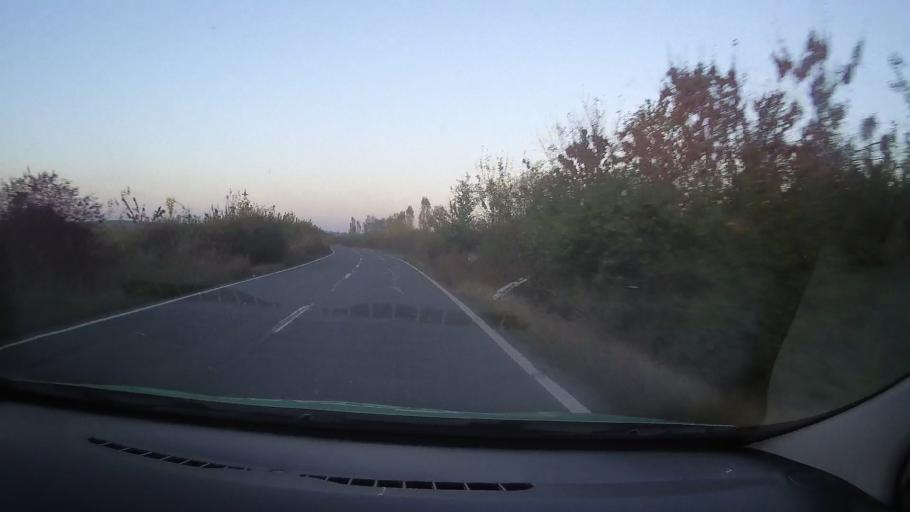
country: RO
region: Timis
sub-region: Comuna Dumbrava
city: Dumbrava
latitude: 45.8337
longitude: 22.1379
